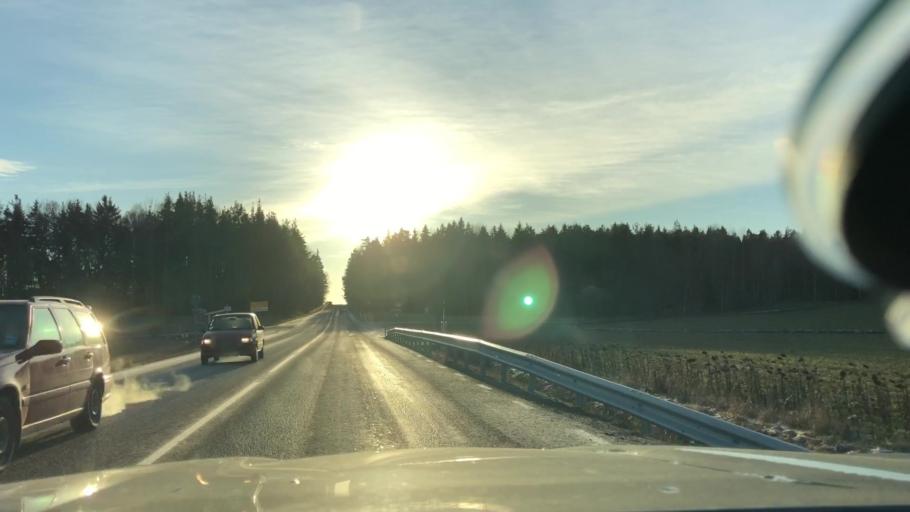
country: SE
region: Stockholm
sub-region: Sodertalje Kommun
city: Pershagen
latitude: 59.0457
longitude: 17.6056
